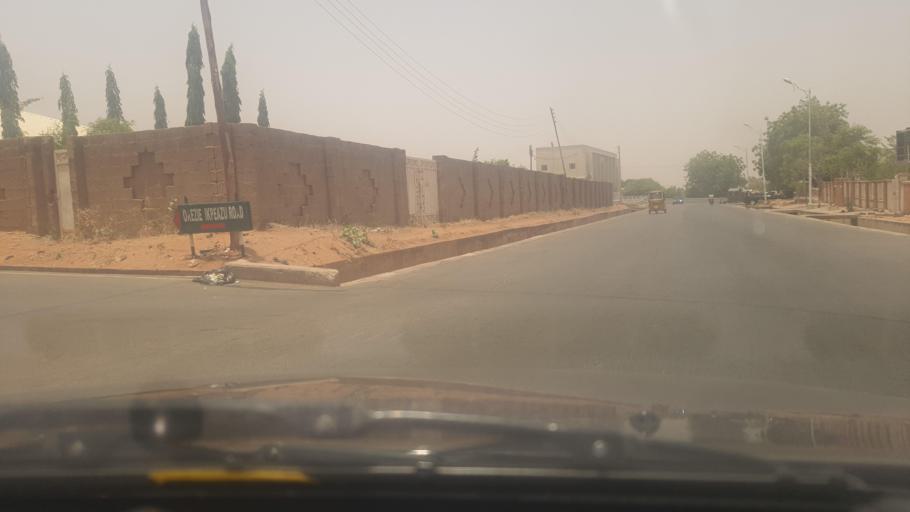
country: NG
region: Gombe
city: Gombe
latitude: 10.3064
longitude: 11.1488
